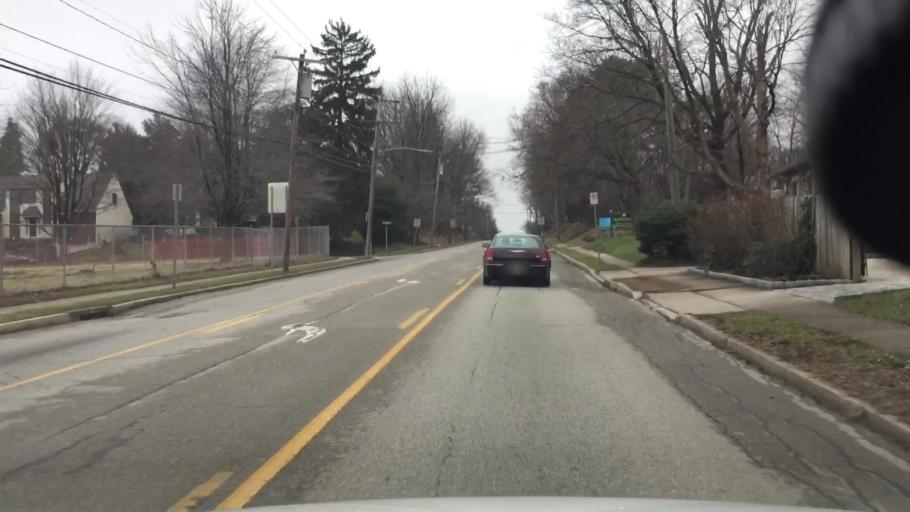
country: US
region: Pennsylvania
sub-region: Montgomery County
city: Flourtown
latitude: 40.0905
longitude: -75.2075
